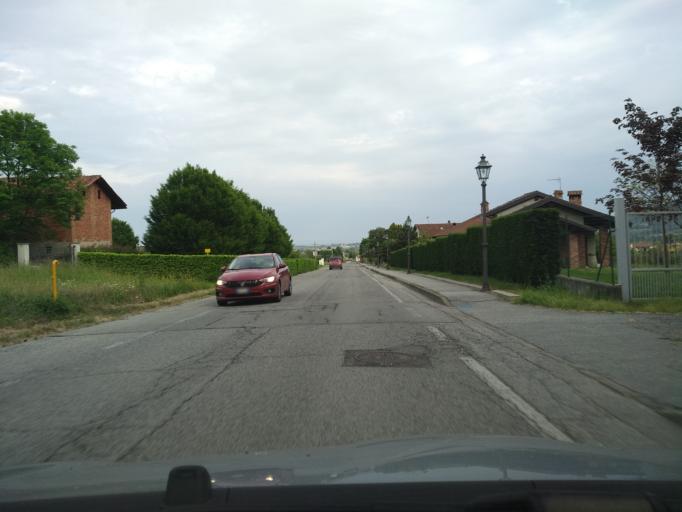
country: IT
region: Piedmont
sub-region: Provincia di Torino
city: Roletto
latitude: 44.9229
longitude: 7.3348
